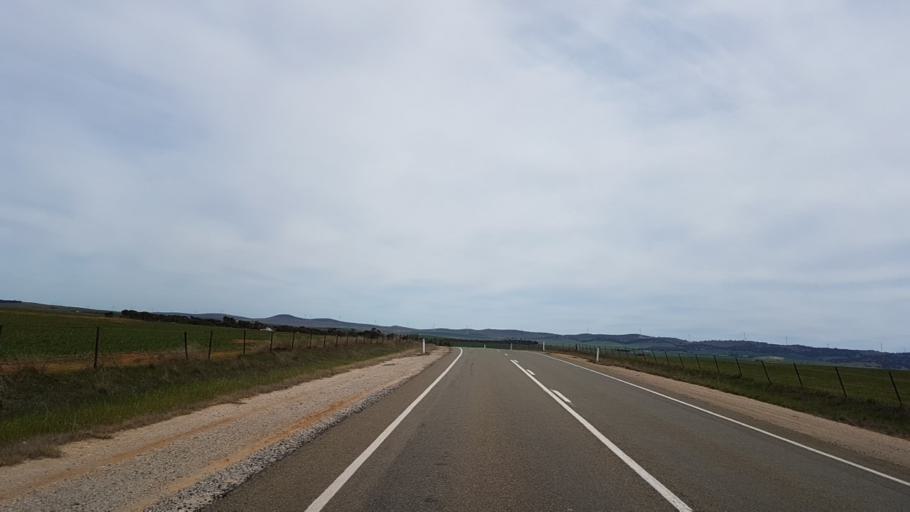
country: AU
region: South Australia
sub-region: Peterborough
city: Peterborough
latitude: -33.0253
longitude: 138.6729
